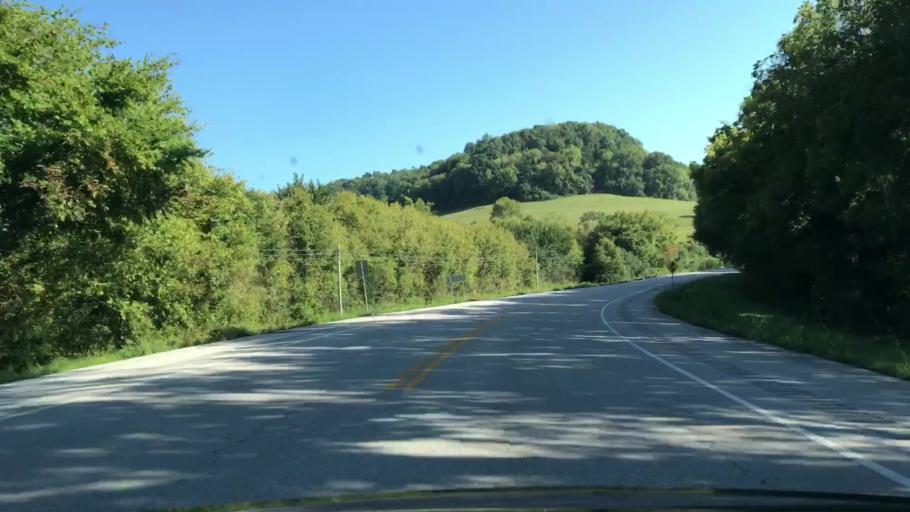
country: US
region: Tennessee
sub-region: Clay County
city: Celina
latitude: 36.4706
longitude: -85.5830
